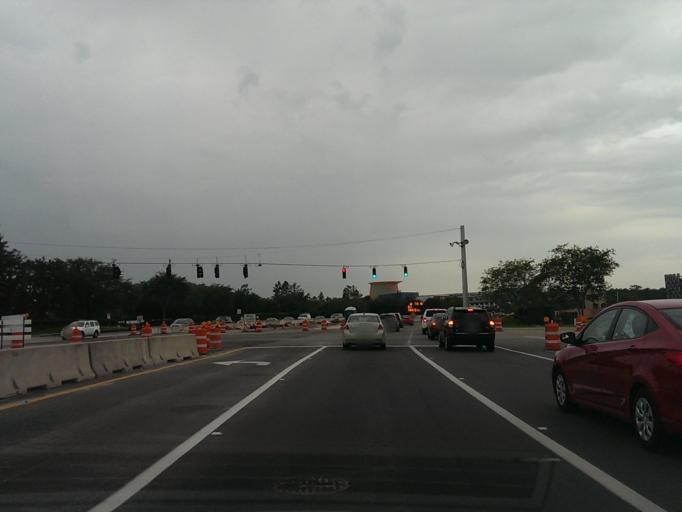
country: US
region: Florida
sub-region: Osceola County
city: Celebration
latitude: 28.3688
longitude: -81.5159
